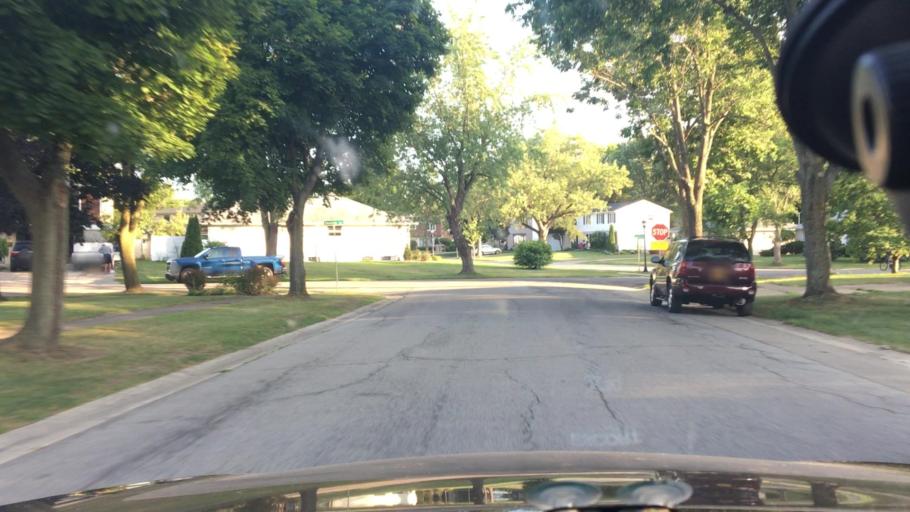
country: US
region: New York
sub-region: Erie County
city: Amherst
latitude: 43.0072
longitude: -78.7621
